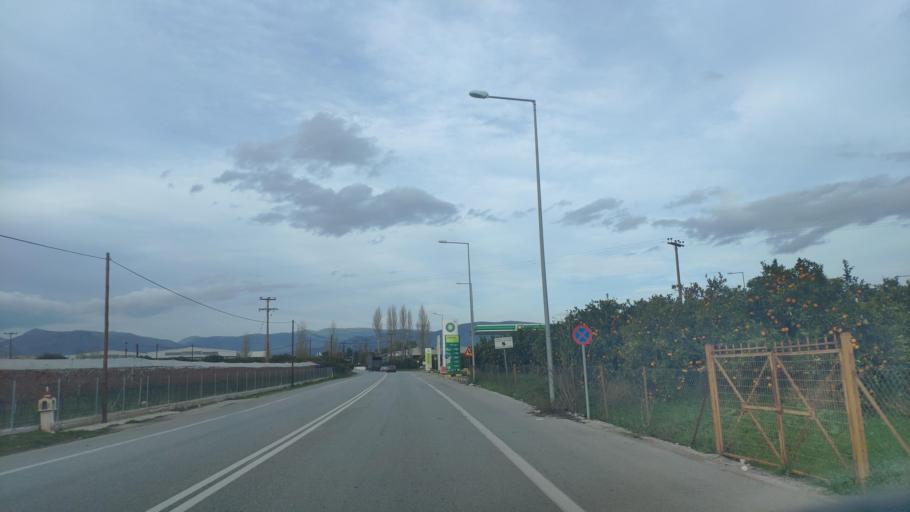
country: GR
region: Peloponnese
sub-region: Nomos Argolidos
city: Nea Tirins
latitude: 37.6097
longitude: 22.8118
